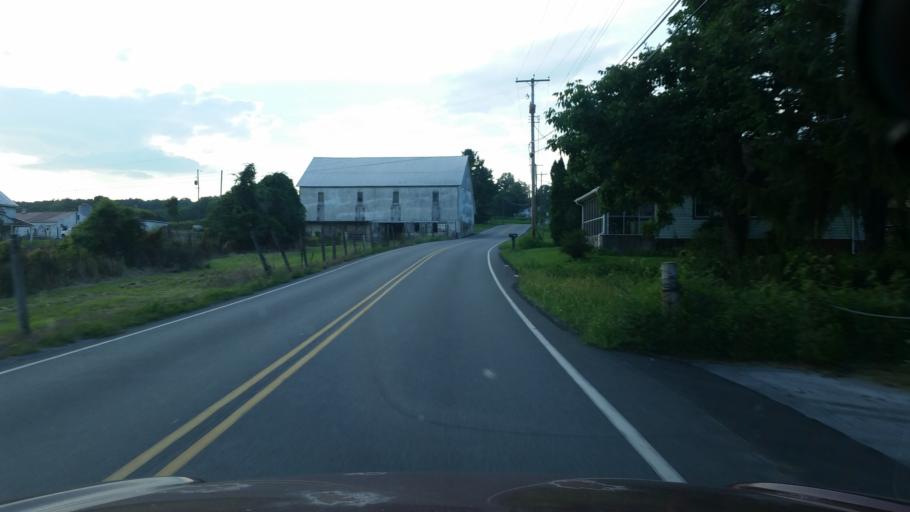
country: US
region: Pennsylvania
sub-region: Lebanon County
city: Campbelltown
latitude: 40.2537
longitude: -76.5484
